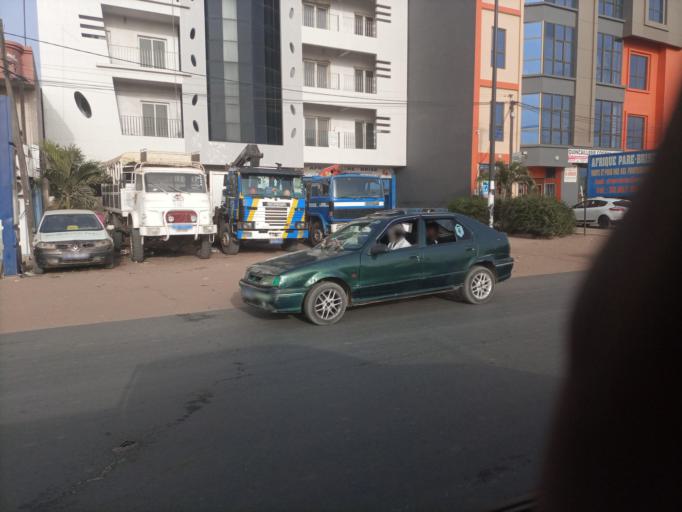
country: SN
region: Thies
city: Warang
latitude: 14.4405
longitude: -16.9787
